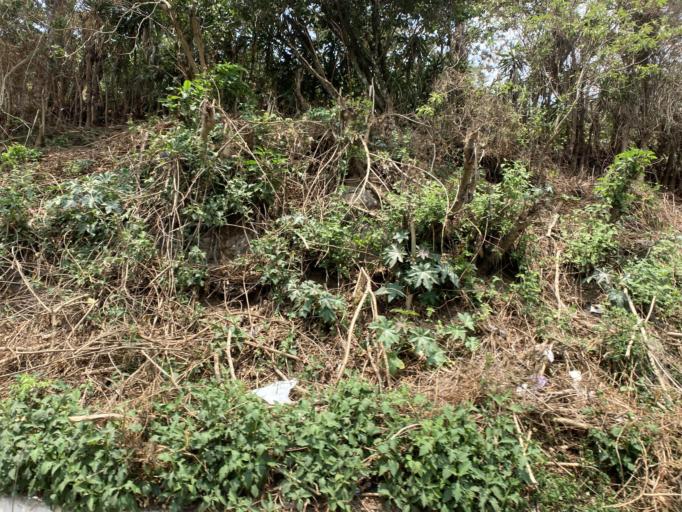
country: GT
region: Guatemala
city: Villa Canales
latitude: 14.3959
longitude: -90.5464
